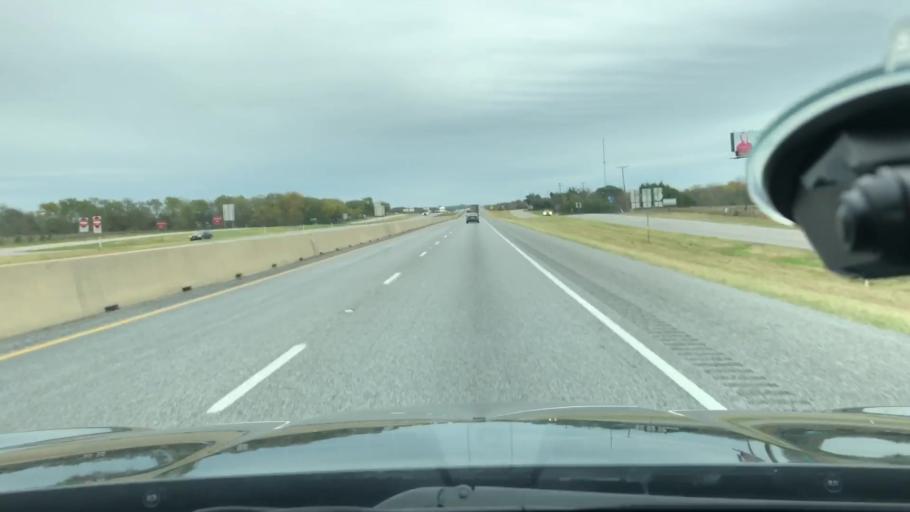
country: US
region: Texas
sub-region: Hunt County
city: Commerce
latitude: 33.1319
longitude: -95.9442
